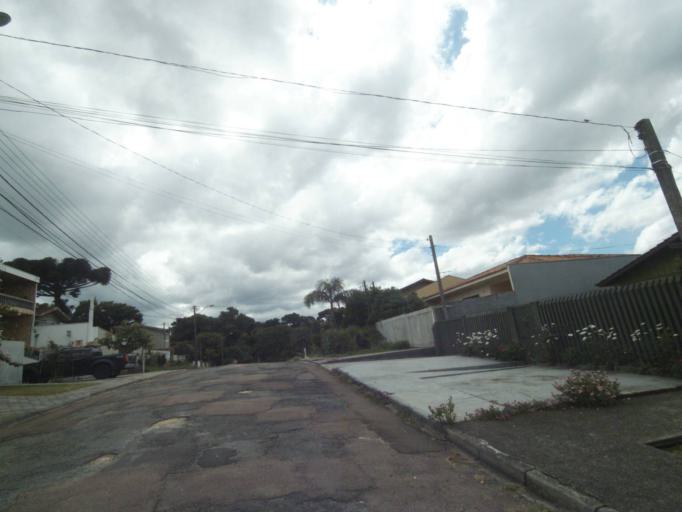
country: BR
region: Parana
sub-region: Curitiba
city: Curitiba
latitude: -25.4319
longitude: -49.3215
